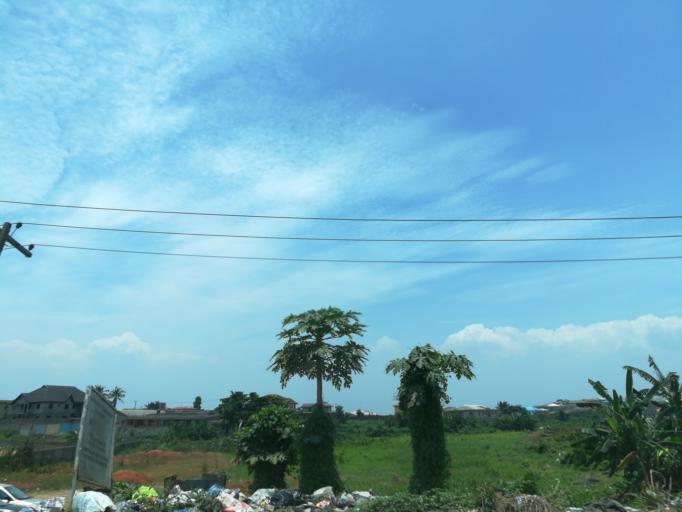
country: NG
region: Lagos
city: Ebute Ikorodu
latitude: 6.6052
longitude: 3.4950
